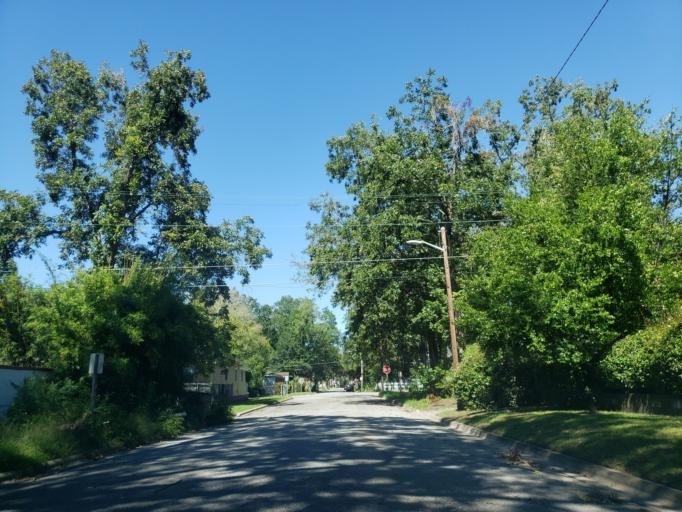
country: US
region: Georgia
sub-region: Chatham County
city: Savannah
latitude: 32.0533
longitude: -81.1108
